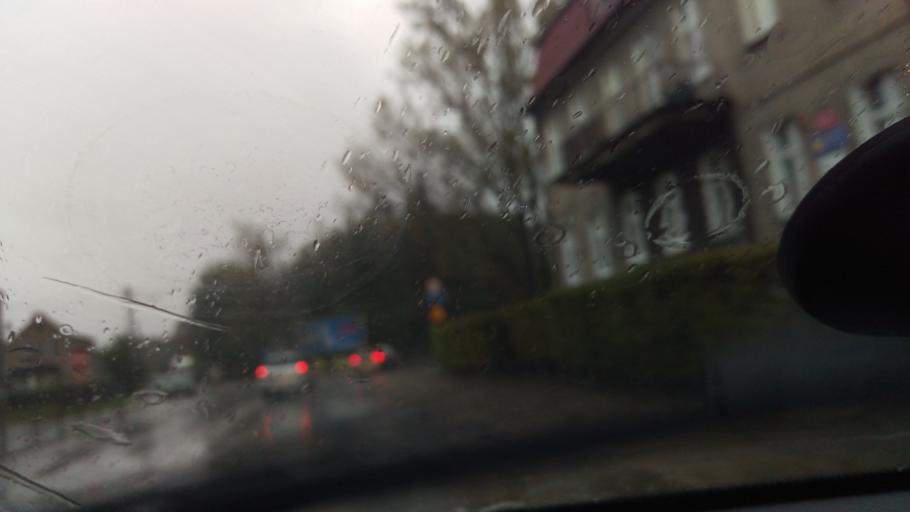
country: PL
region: West Pomeranian Voivodeship
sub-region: Szczecin
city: Szczecin
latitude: 53.3939
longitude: 14.6629
